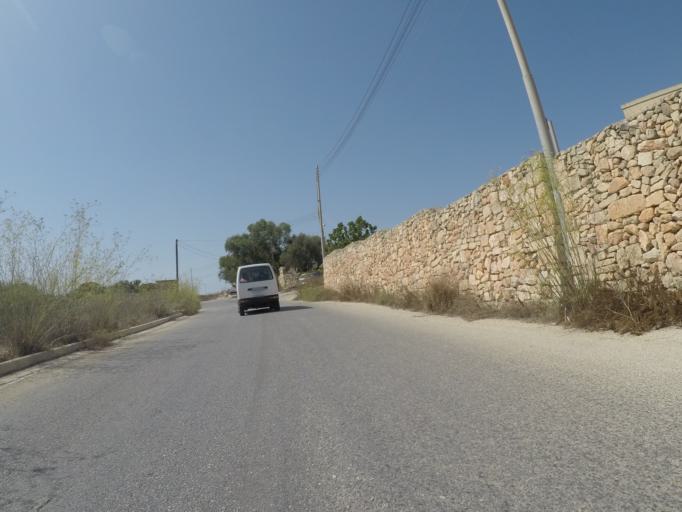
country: MT
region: L-Imgarr
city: Imgarr
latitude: 35.9273
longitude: 14.3776
